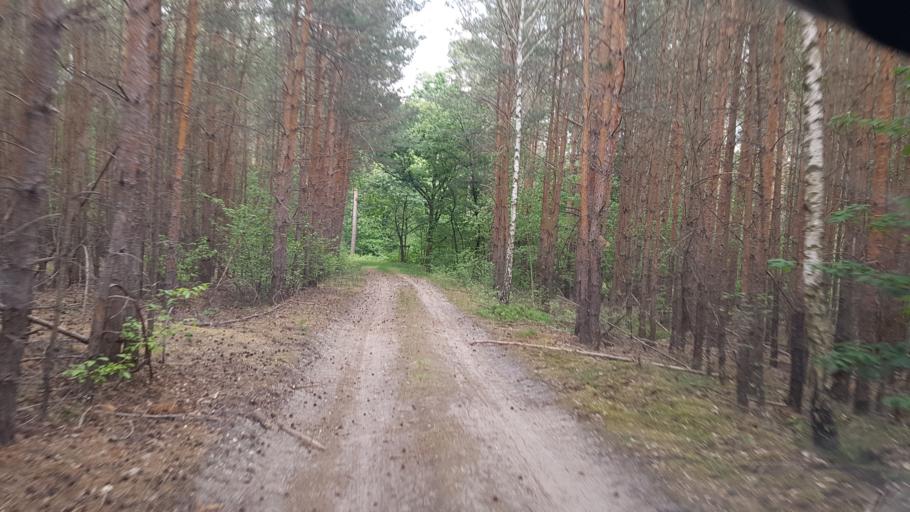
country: DE
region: Brandenburg
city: Hohenleipisch
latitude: 51.5089
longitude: 13.5664
